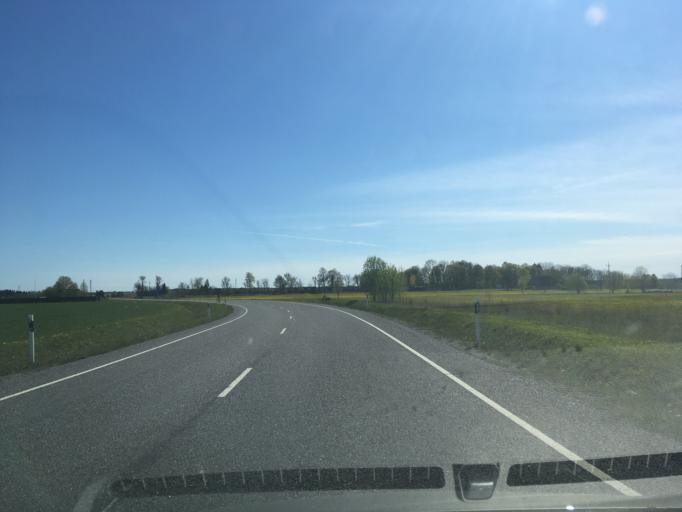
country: EE
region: Harju
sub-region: Rae vald
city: Vaida
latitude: 59.2595
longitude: 25.0187
